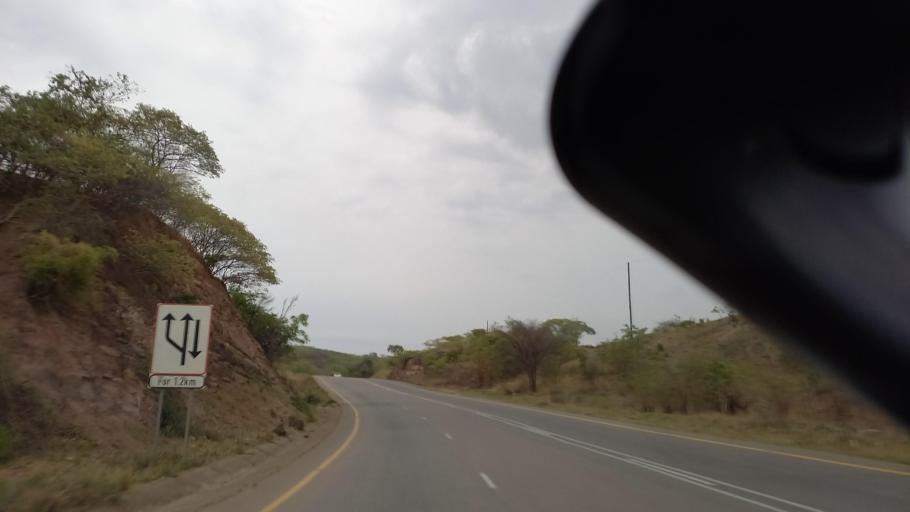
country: ZW
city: Chirundu
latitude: -16.0506
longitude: 28.4979
